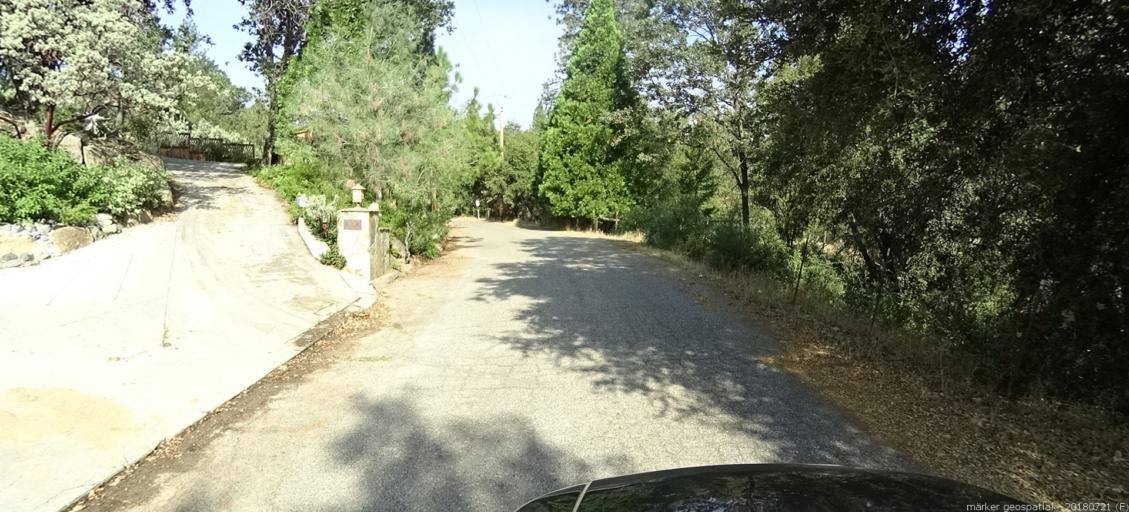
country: US
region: California
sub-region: Madera County
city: Oakhurst
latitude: 37.2506
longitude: -119.5254
